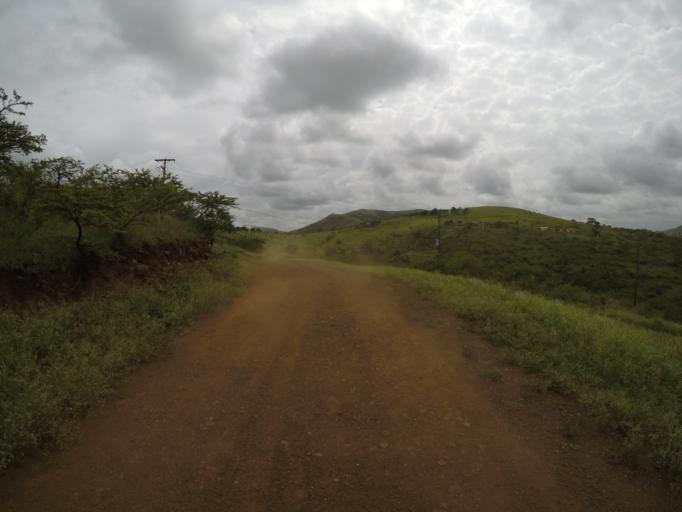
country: ZA
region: KwaZulu-Natal
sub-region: uThungulu District Municipality
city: Empangeni
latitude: -28.6224
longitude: 31.8910
